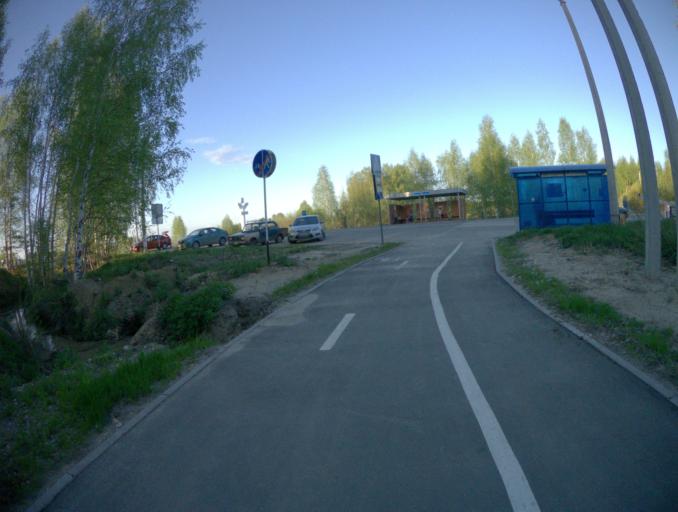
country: RU
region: Vladimir
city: Raduzhnyy
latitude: 56.0061
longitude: 40.3059
